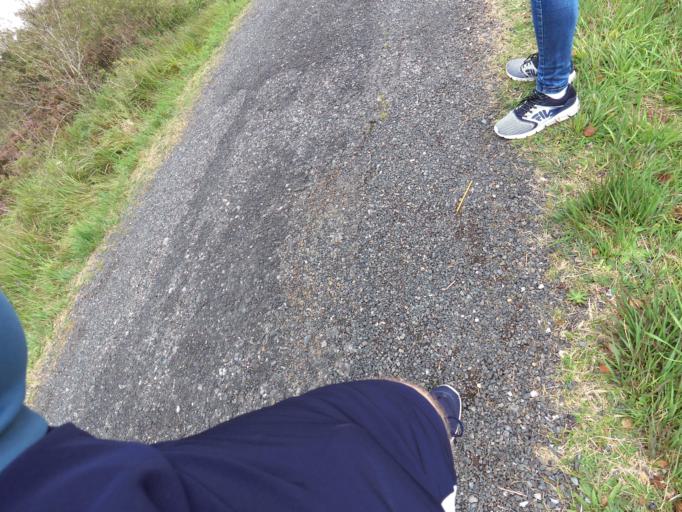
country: IE
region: Leinster
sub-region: Uibh Fhaili
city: Ferbane
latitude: 53.2175
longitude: -7.7318
